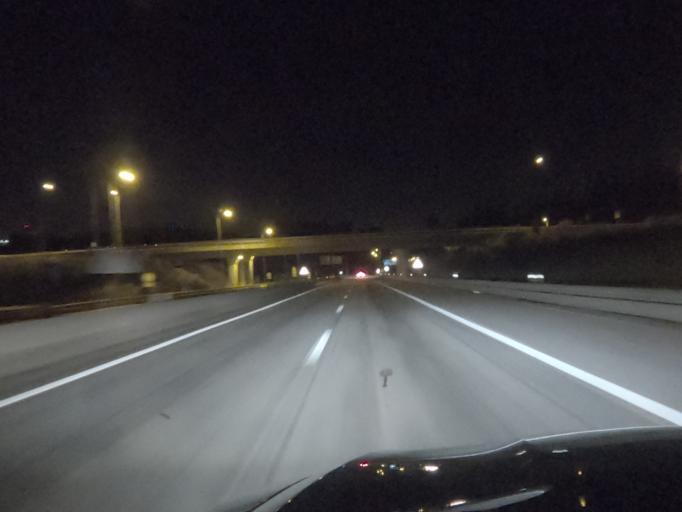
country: PT
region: Porto
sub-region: Vila Nova de Gaia
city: Perozinho
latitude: 41.0841
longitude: -8.5754
